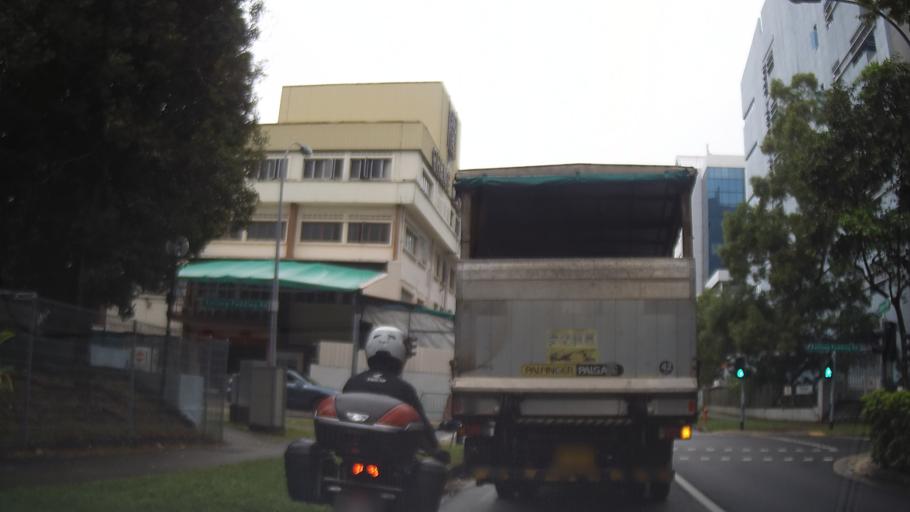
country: SG
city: Singapore
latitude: 1.3295
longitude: 103.8772
